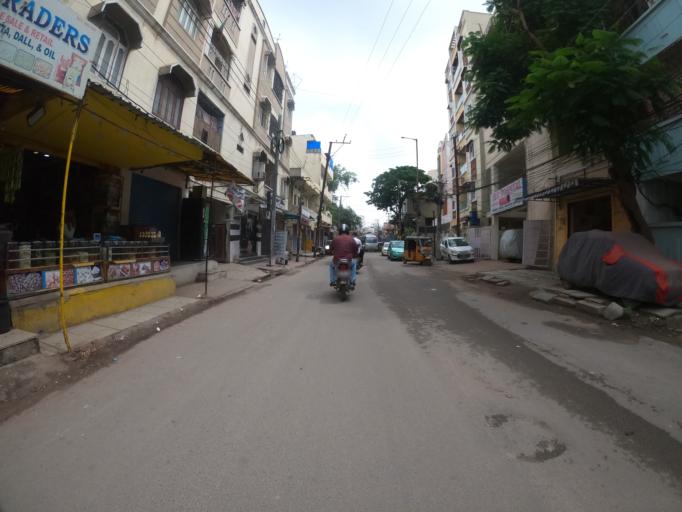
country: IN
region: Telangana
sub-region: Hyderabad
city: Hyderabad
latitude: 17.3956
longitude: 78.4174
